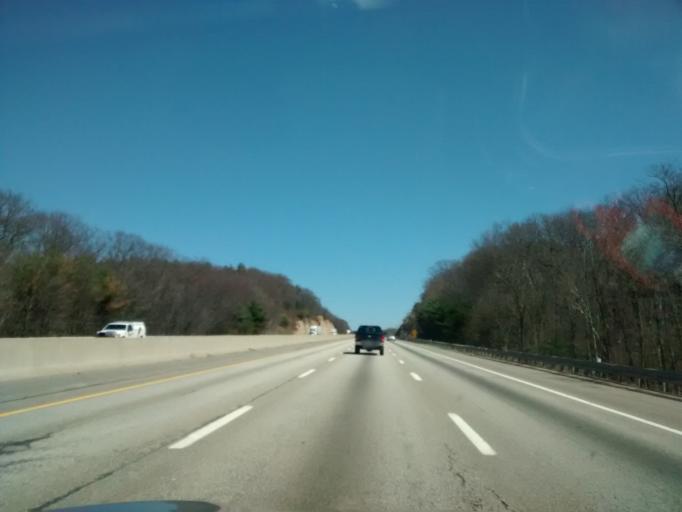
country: US
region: Massachusetts
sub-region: Worcester County
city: Grafton
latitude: 42.2280
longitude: -71.6477
